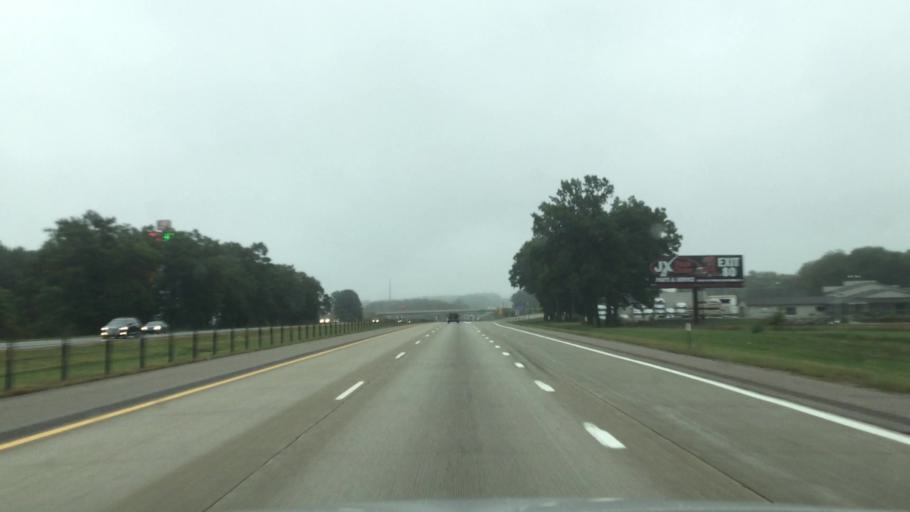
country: US
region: Michigan
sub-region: Van Buren County
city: Mattawan
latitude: 42.2223
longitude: -85.7919
